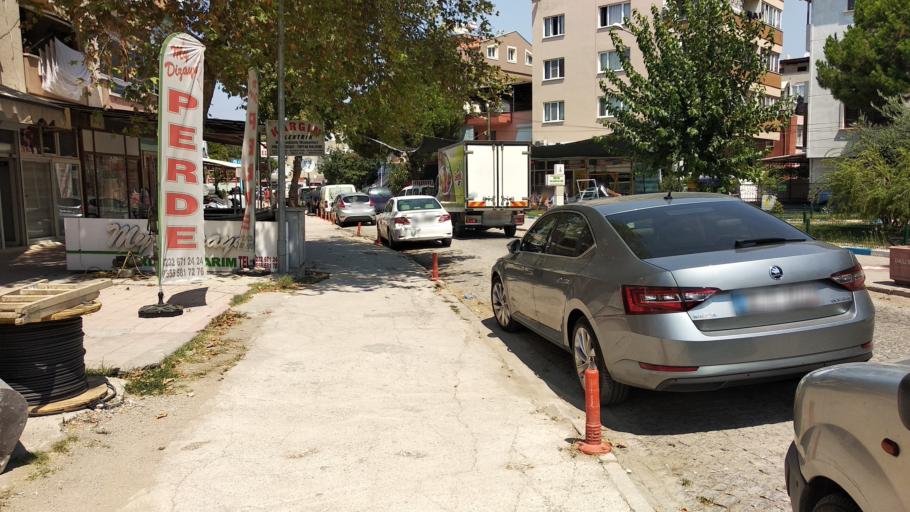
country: TR
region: Izmir
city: Dikili
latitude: 39.0729
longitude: 26.8902
